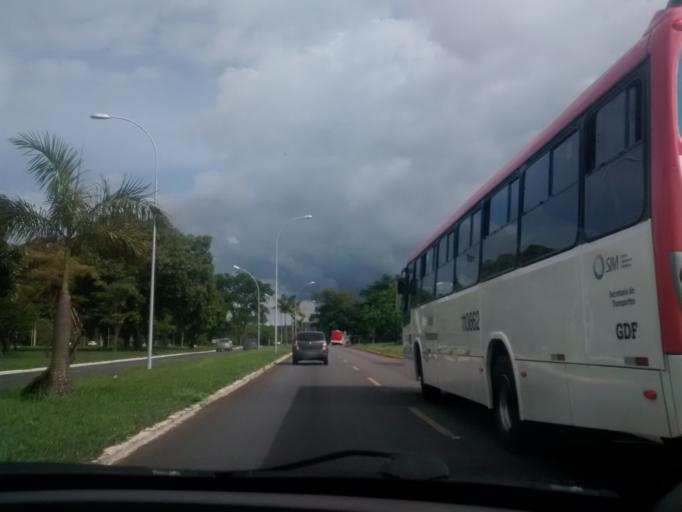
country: BR
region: Federal District
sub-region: Brasilia
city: Brasilia
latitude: -15.7605
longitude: -47.8839
